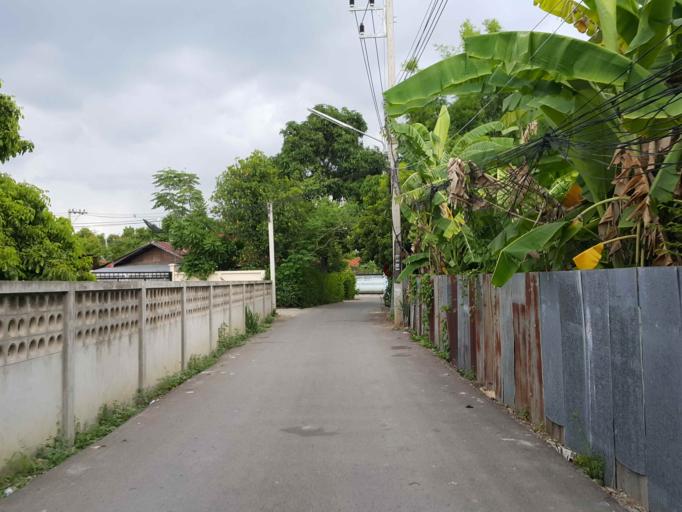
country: TH
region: Chiang Mai
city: Saraphi
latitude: 18.7124
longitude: 99.0346
